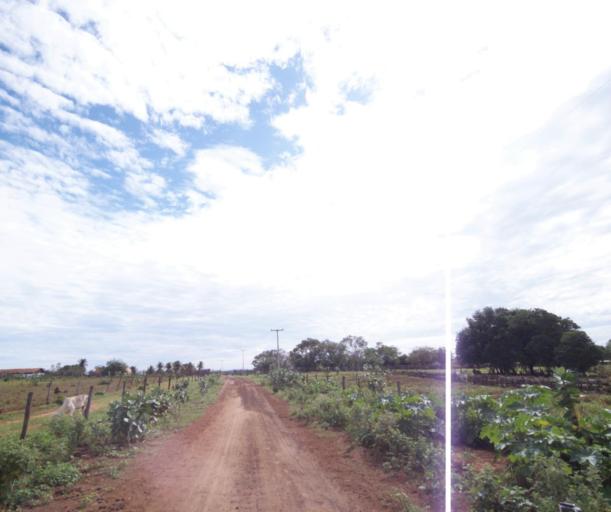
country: BR
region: Bahia
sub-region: Carinhanha
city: Carinhanha
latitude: -14.2390
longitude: -44.4101
